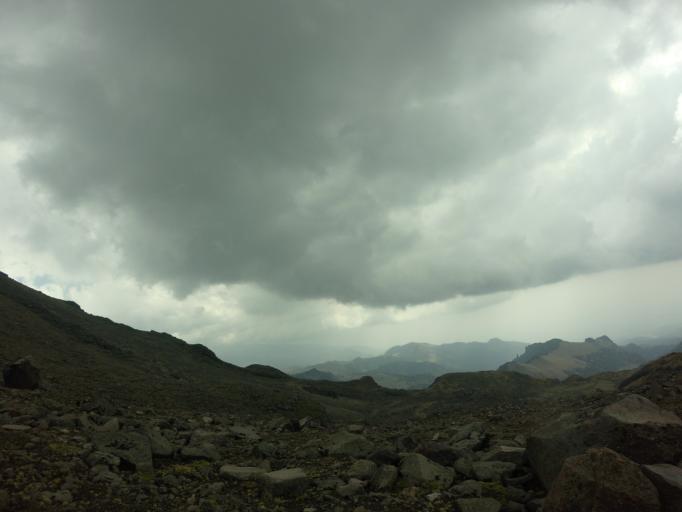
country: MX
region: Mexico
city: Amecameca de Juarez
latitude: 19.1566
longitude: -98.6425
